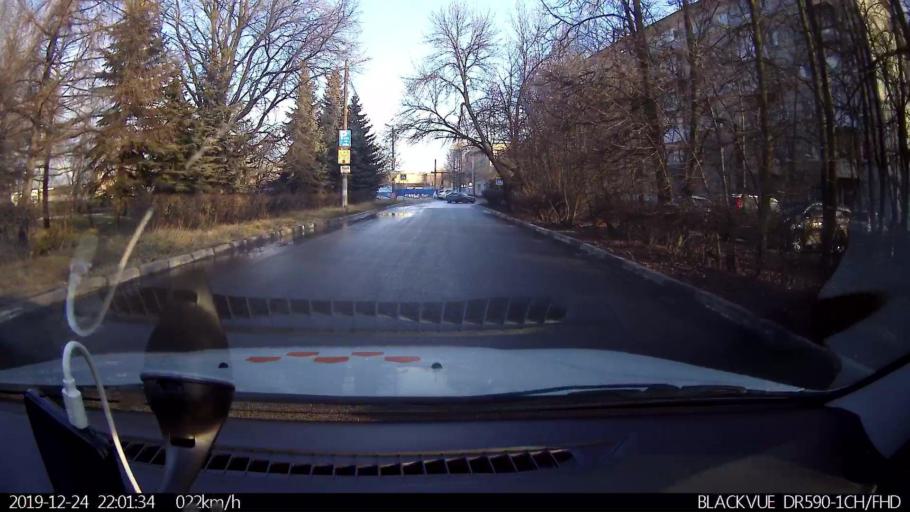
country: RU
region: Nizjnij Novgorod
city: Nizhniy Novgorod
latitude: 56.3229
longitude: 43.8840
